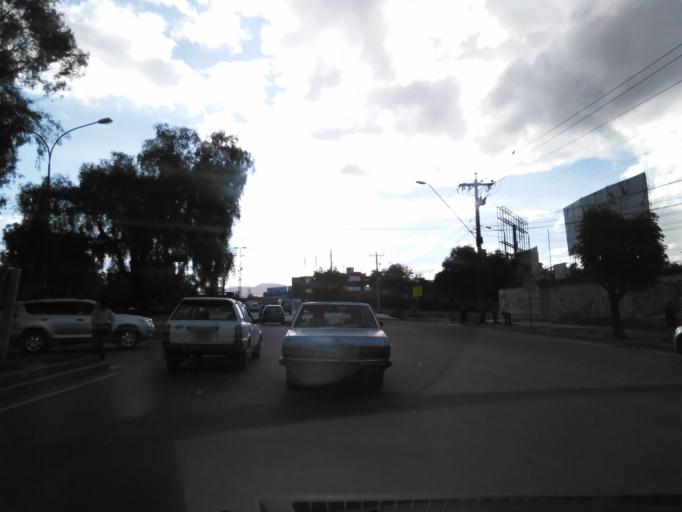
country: BO
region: Cochabamba
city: Cochabamba
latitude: -17.3941
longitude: -66.1683
